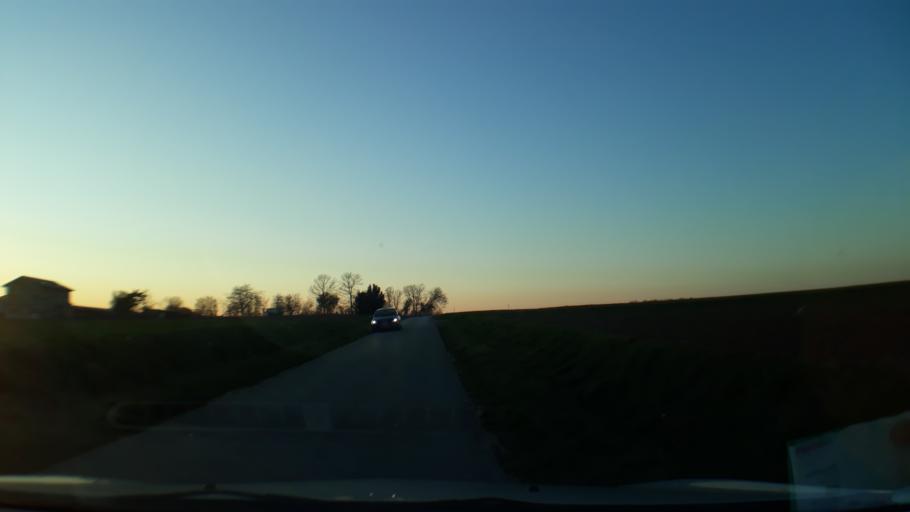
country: DE
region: North Rhine-Westphalia
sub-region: Regierungsbezirk Koln
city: Vettweiss
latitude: 50.7075
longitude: 6.6178
